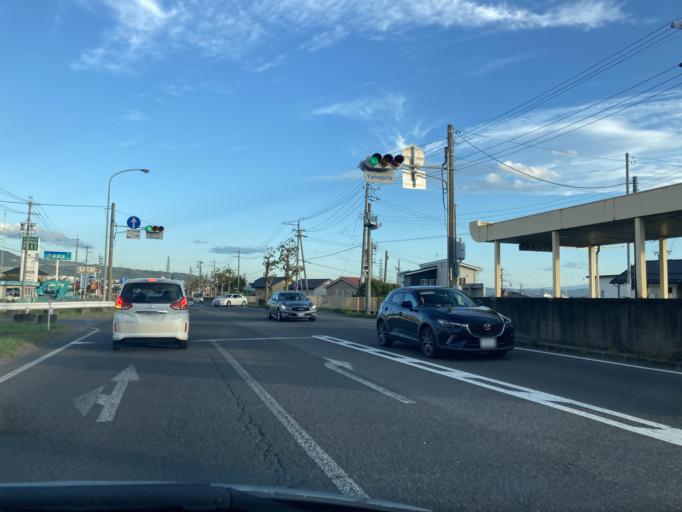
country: JP
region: Nagano
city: Ueda
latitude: 36.4110
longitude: 138.2633
